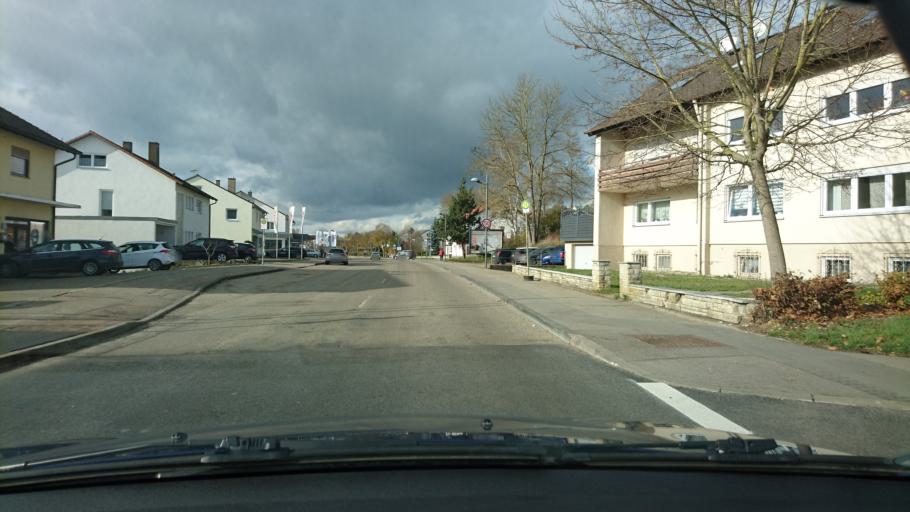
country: DE
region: Baden-Wuerttemberg
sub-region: Regierungsbezirk Stuttgart
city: Neresheim
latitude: 48.7547
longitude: 10.3304
